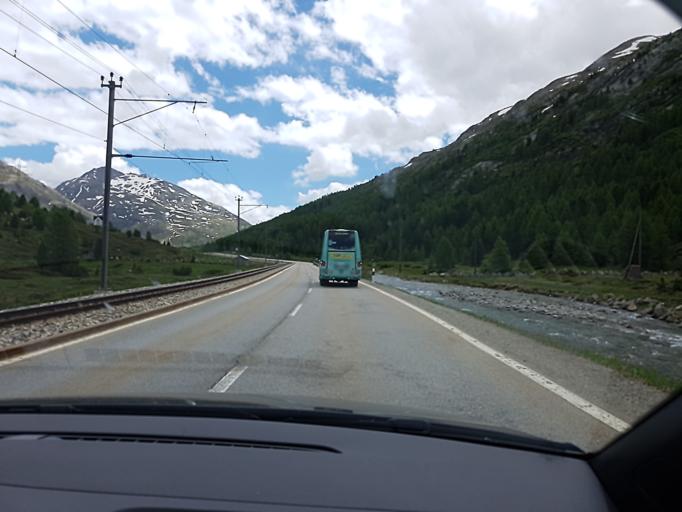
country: CH
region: Grisons
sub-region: Maloja District
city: Pontresina
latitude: 46.4505
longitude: 9.9543
